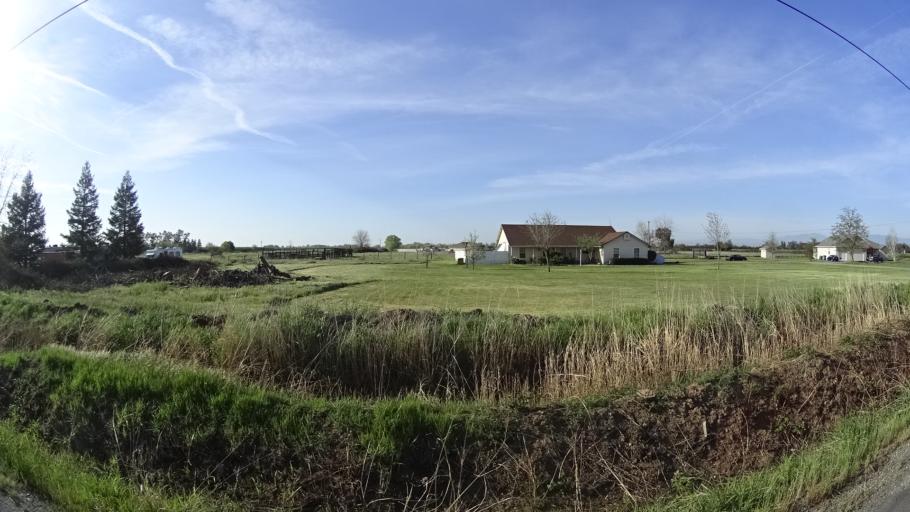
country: US
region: California
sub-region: Glenn County
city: Orland
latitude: 39.7153
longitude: -122.2282
